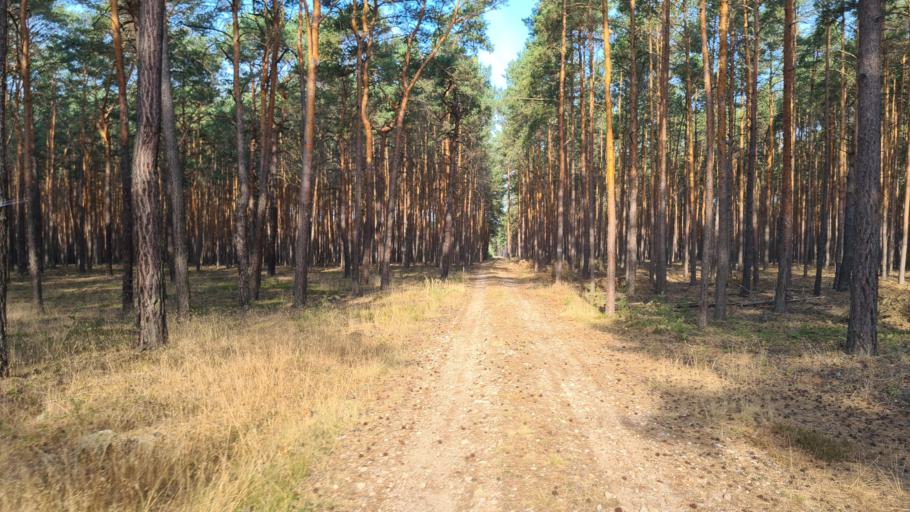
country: DE
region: Brandenburg
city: Crinitz
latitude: 51.6728
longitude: 13.7755
